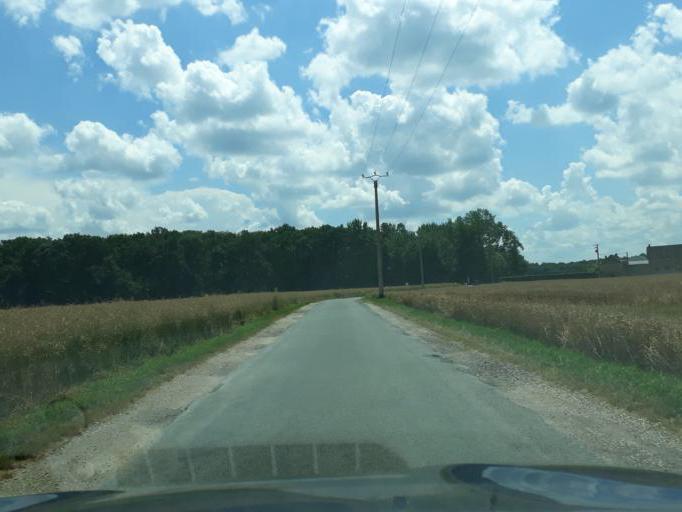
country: FR
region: Centre
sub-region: Departement du Loiret
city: Chevilly
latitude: 48.0228
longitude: 1.9220
